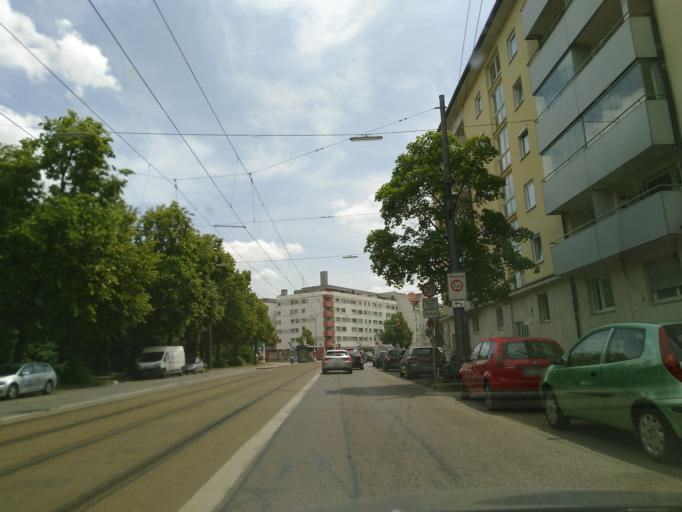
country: DE
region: Bavaria
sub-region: Upper Bavaria
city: Munich
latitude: 48.1157
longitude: 11.5917
